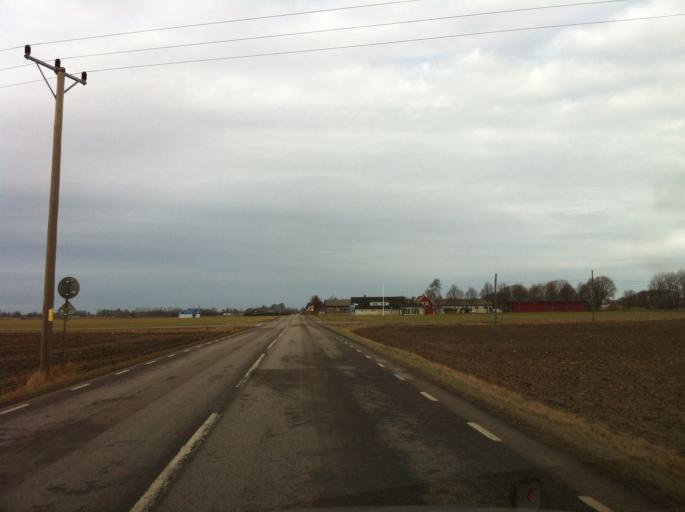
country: SE
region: Skane
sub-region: Angelholms Kommun
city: Strovelstorp
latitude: 56.1605
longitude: 12.8614
